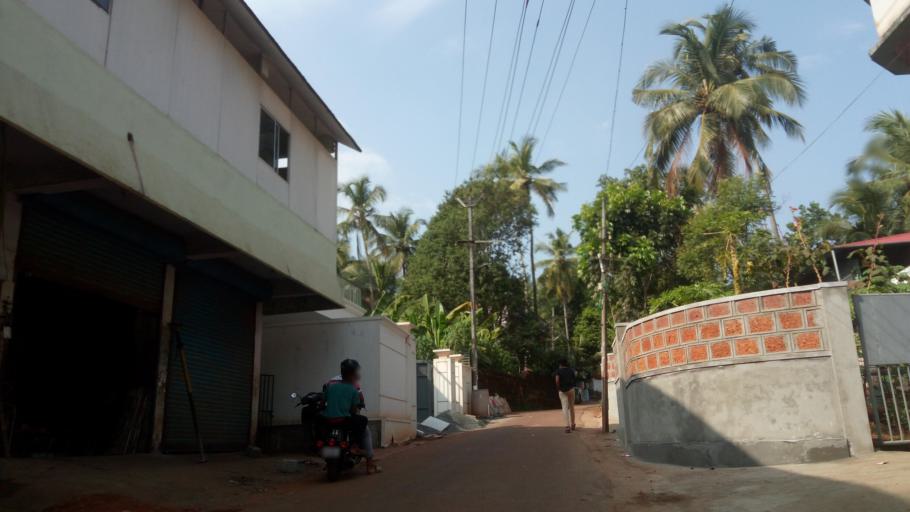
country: IN
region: Kerala
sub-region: Malappuram
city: Malappuram
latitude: 10.9961
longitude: 75.9997
